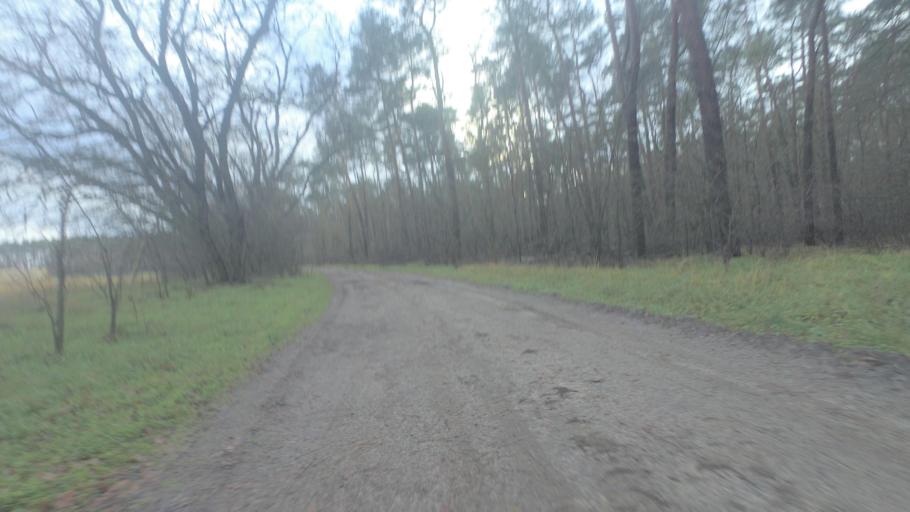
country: DE
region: Brandenburg
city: Ludwigsfelde
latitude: 52.2644
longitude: 13.2381
